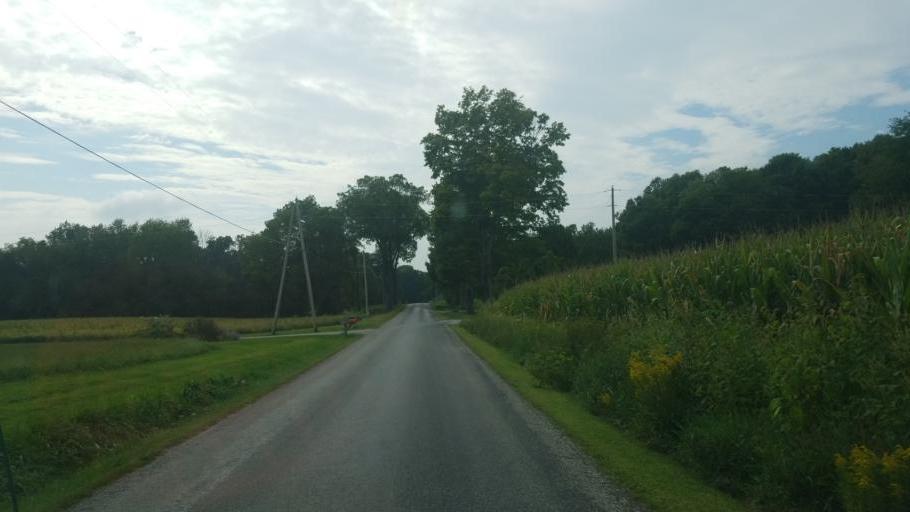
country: US
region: Ohio
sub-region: Wayne County
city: Wooster
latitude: 40.9011
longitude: -81.9974
